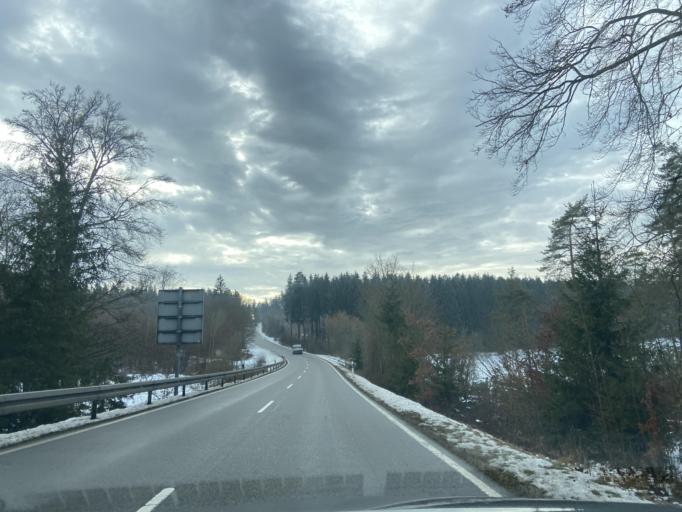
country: DE
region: Baden-Wuerttemberg
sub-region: Tuebingen Region
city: Bingen
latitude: 48.1480
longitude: 9.2598
